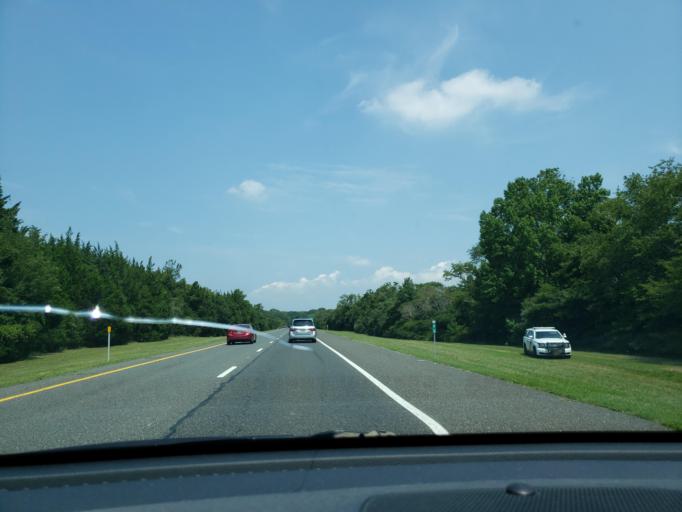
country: US
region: New Jersey
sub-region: Cape May County
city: Erma
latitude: 38.9878
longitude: -74.8822
